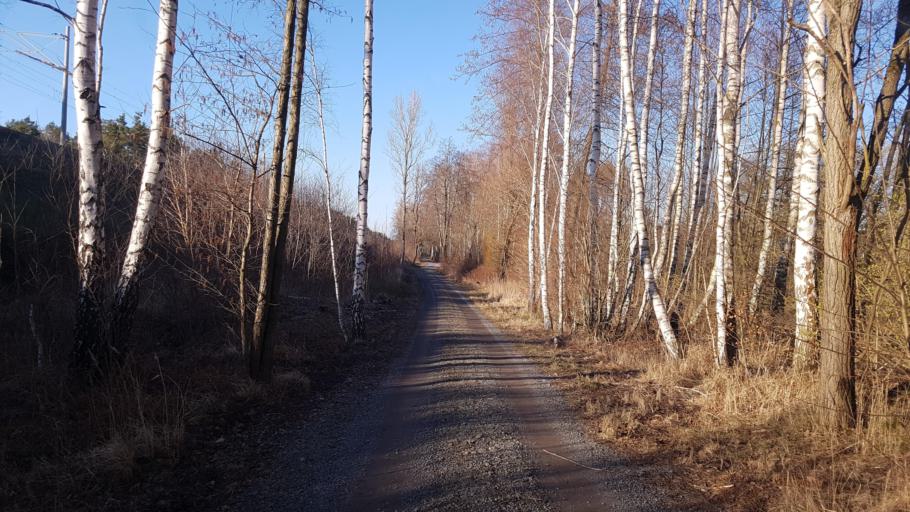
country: DE
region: Brandenburg
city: Hohenleipisch
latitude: 51.5090
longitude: 13.5769
